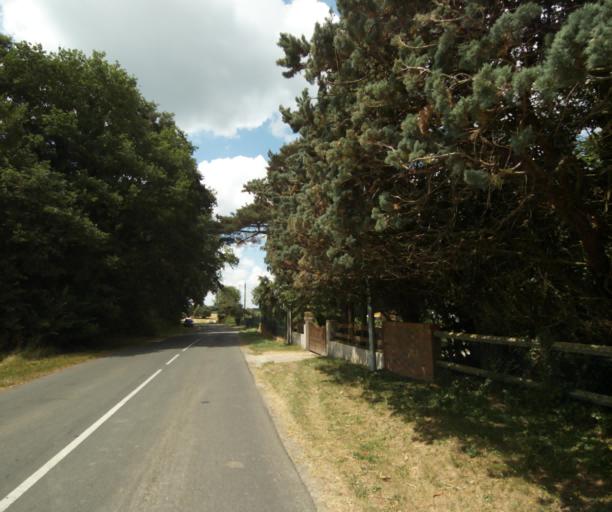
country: FR
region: Ile-de-France
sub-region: Departement de Seine-et-Marne
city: Hericy
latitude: 48.4417
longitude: 2.7919
